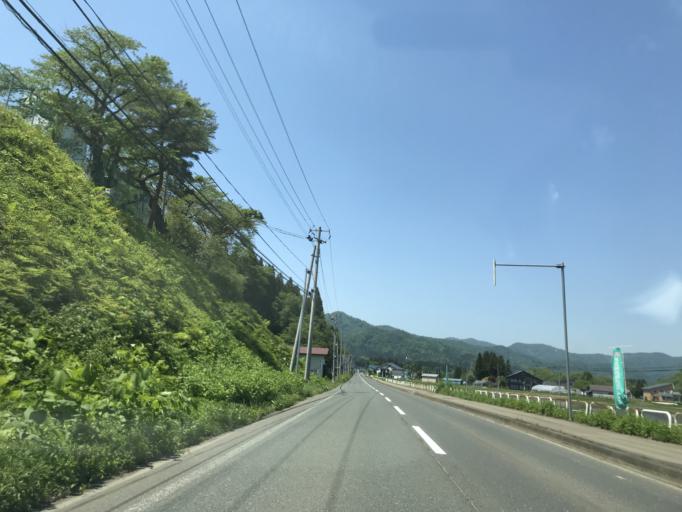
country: JP
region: Akita
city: Yokotemachi
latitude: 39.4032
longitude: 140.7544
